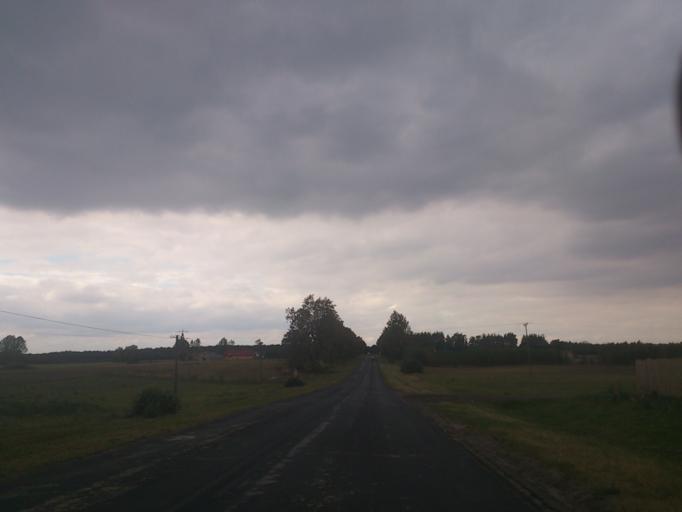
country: PL
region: Kujawsko-Pomorskie
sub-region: Powiat golubsko-dobrzynski
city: Golub-Dobrzyn
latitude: 53.0692
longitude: 19.0702
